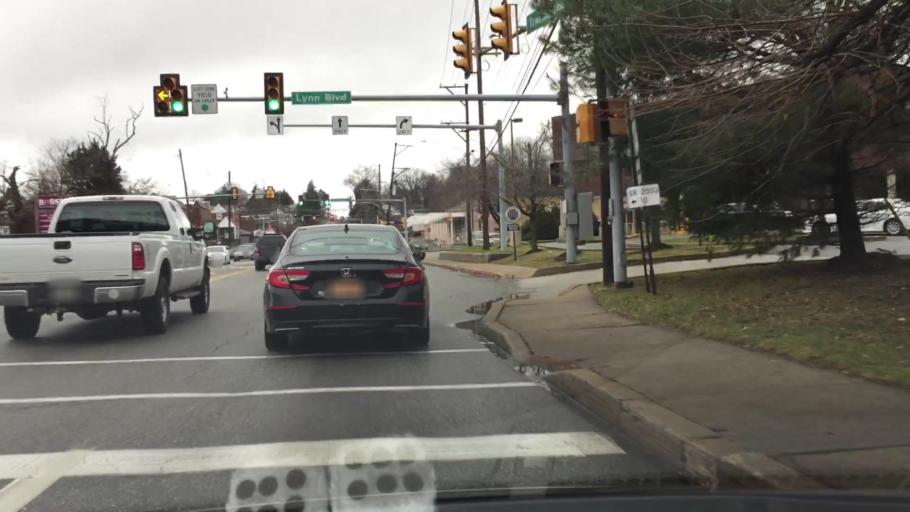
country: US
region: Pennsylvania
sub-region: Montgomery County
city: Penn Wynne
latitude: 39.9727
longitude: -75.2855
